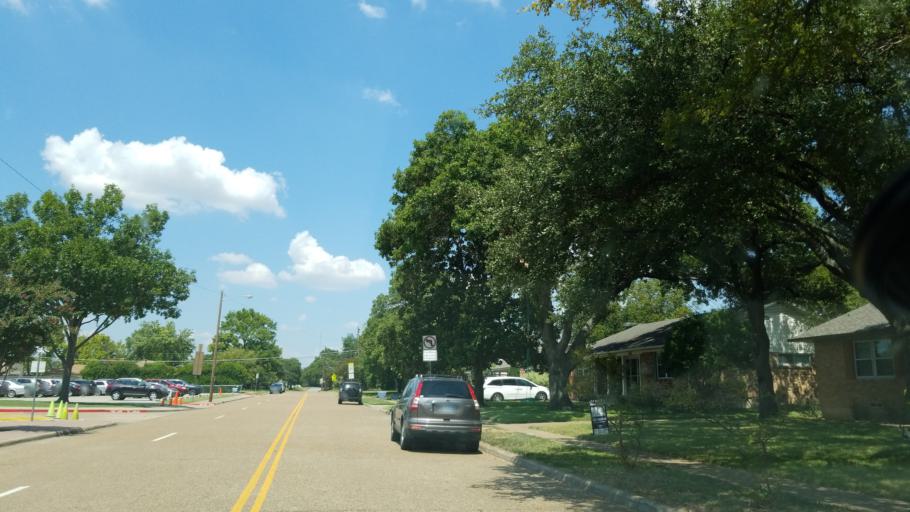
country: US
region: Texas
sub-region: Dallas County
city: Richardson
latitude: 32.8839
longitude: -96.7071
